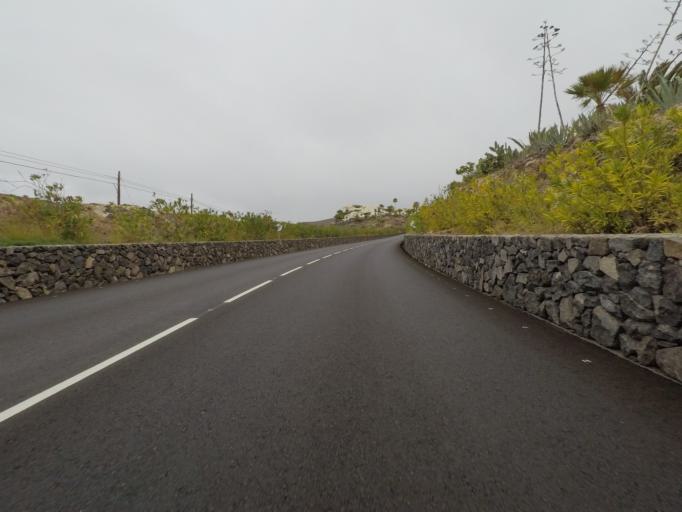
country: ES
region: Canary Islands
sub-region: Provincia de Santa Cruz de Tenerife
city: Alajero
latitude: 28.0381
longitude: -17.1953
